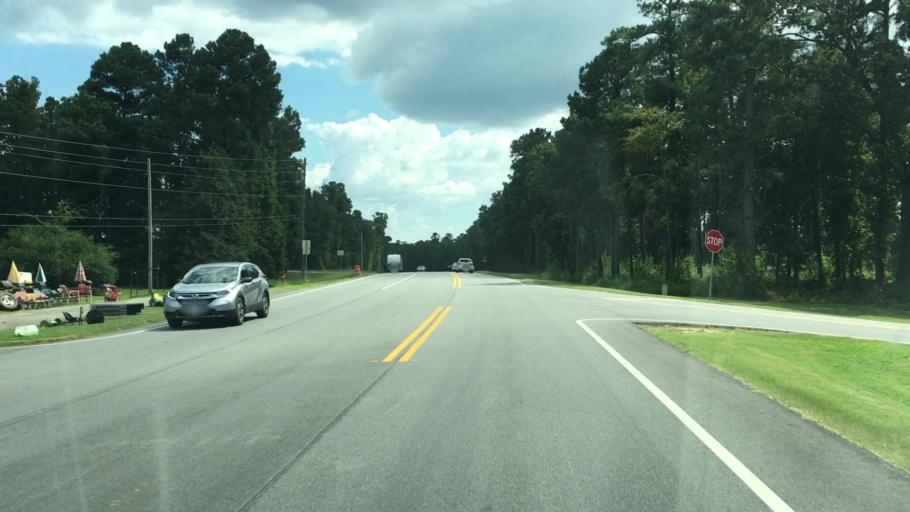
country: US
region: Georgia
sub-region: Putnam County
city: Jefferson
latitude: 33.4175
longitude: -83.3725
